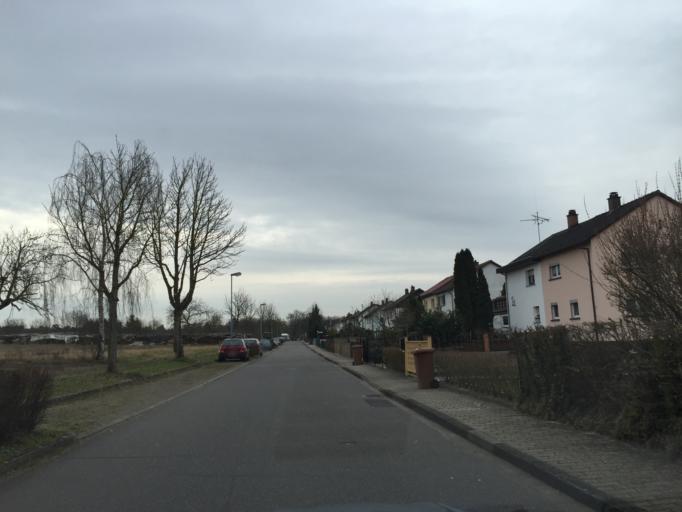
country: DE
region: Baden-Wuerttemberg
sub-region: Karlsruhe Region
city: Oftersheim
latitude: 49.3612
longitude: 8.5833
